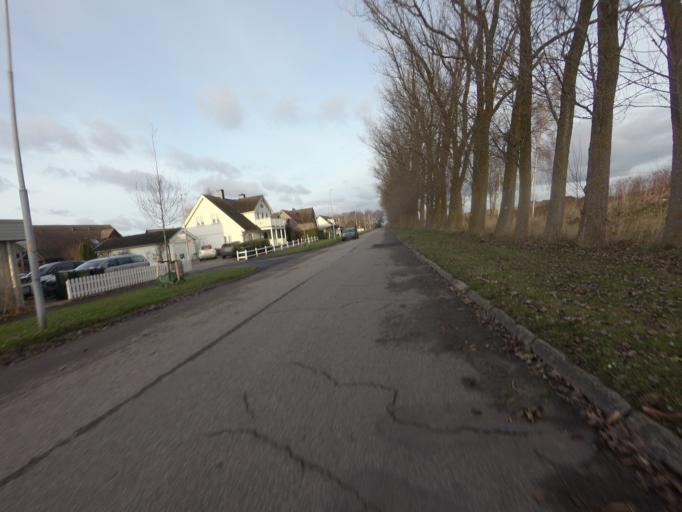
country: SE
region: Skane
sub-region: Hoganas Kommun
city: Hoganas
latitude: 56.1805
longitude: 12.5758
